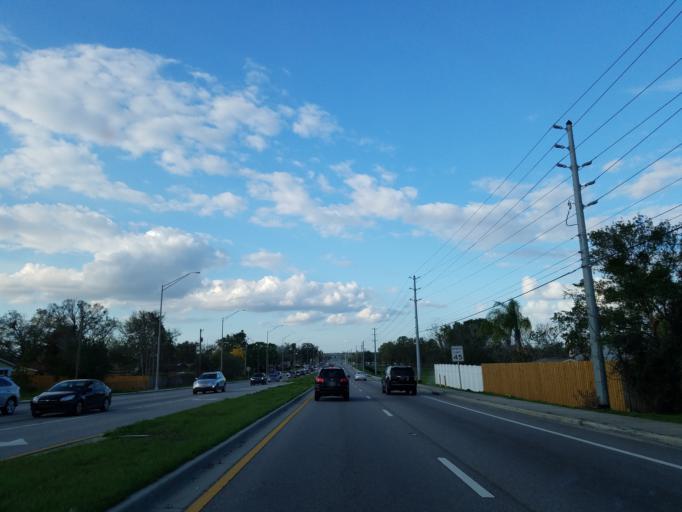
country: US
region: Florida
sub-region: Polk County
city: Lakeland Highlands
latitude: 27.9751
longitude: -81.9238
